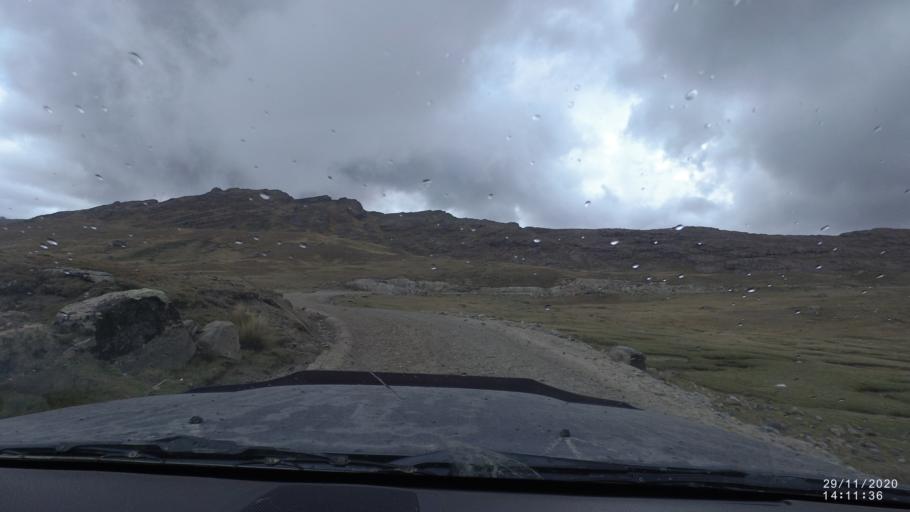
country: BO
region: Cochabamba
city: Sipe Sipe
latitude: -17.2351
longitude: -66.3920
